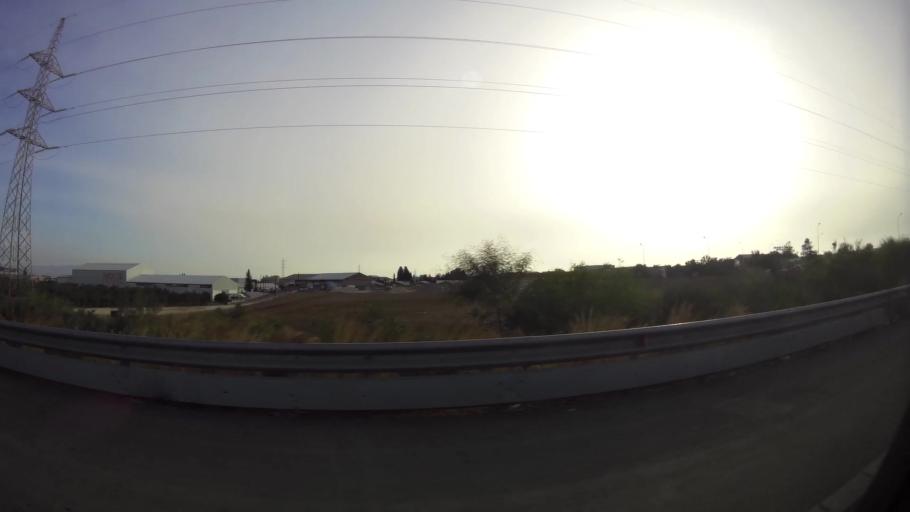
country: CY
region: Lefkosia
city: Geri
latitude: 35.0894
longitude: 33.3752
